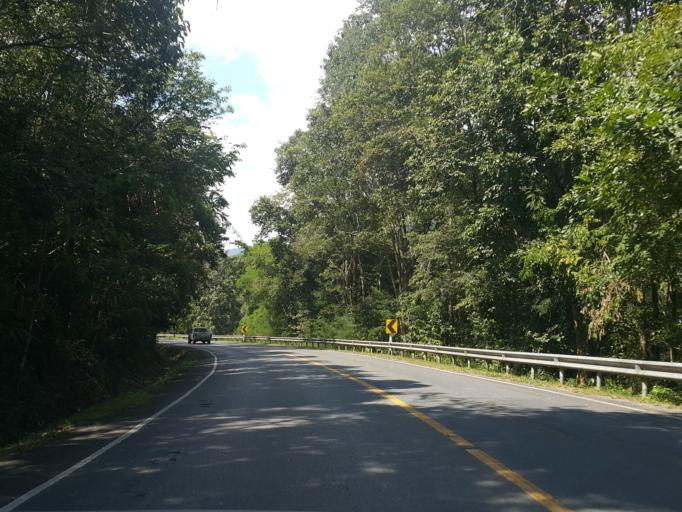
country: TH
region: Chiang Mai
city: Chom Thong
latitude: 18.5284
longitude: 98.6190
